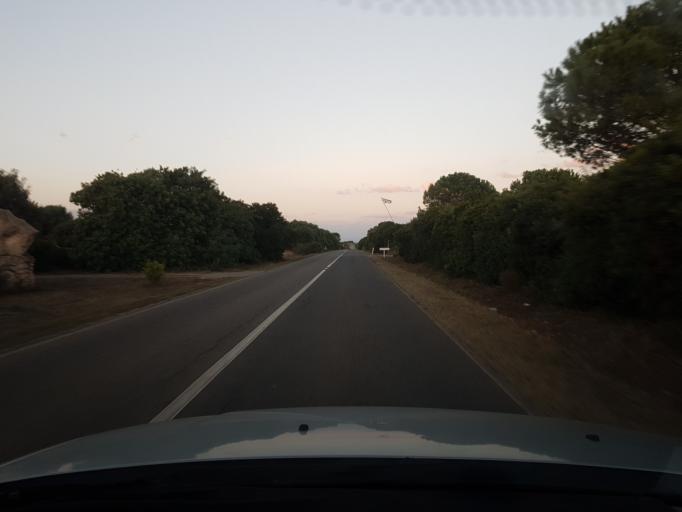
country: IT
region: Sardinia
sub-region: Provincia di Oristano
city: Riola Sardo
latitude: 40.0213
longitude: 8.4572
